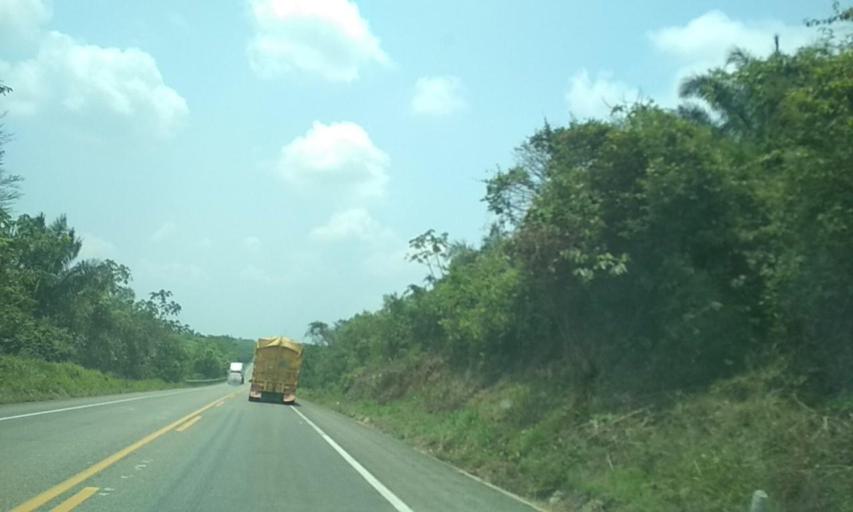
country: MX
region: Tabasco
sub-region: Huimanguillo
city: Francisco Rueda
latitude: 17.7331
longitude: -93.9712
